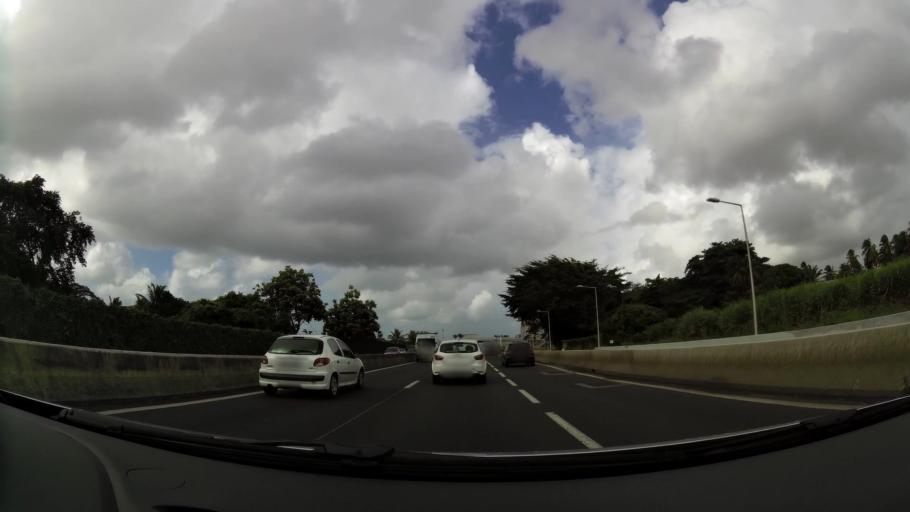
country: MQ
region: Martinique
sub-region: Martinique
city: Le Lamentin
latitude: 14.5963
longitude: -60.9915
